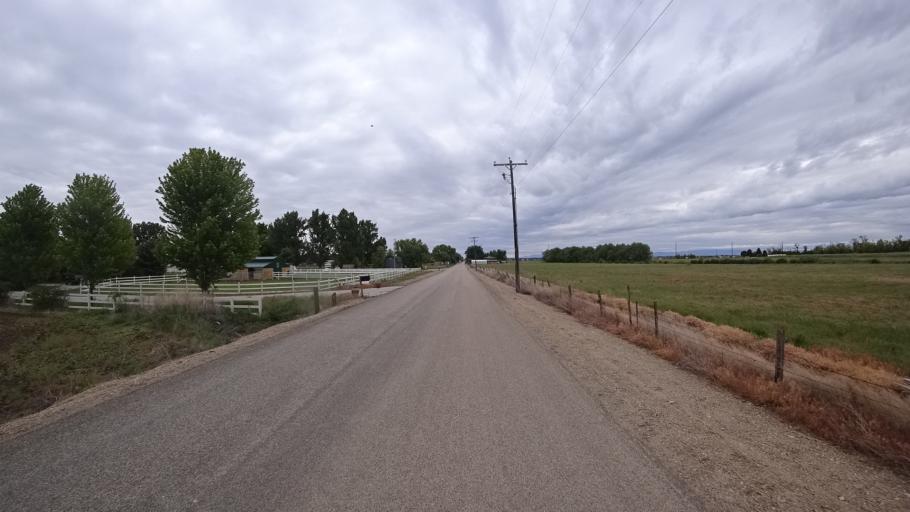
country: US
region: Idaho
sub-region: Ada County
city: Eagle
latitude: 43.7246
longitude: -116.4134
